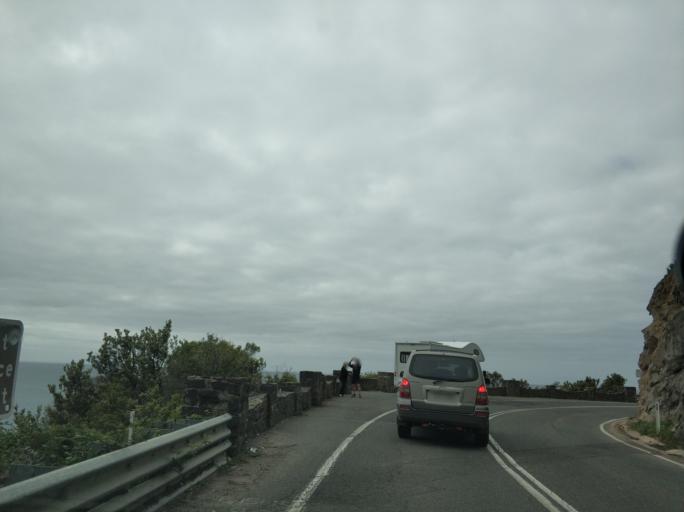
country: AU
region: Victoria
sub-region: Surf Coast
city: Anglesea
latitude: -38.5869
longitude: 143.9337
